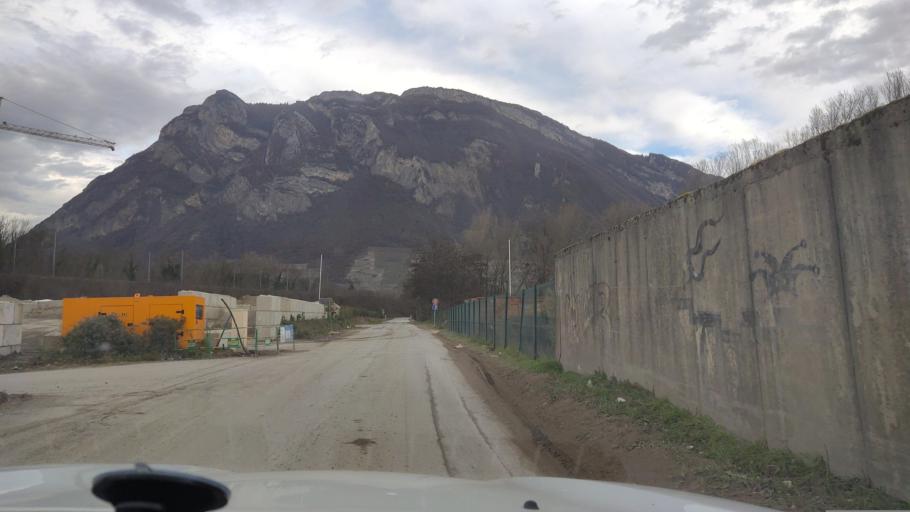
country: FR
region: Rhone-Alpes
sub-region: Departement de la Savoie
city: Montmelian
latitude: 45.4914
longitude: 6.0426
